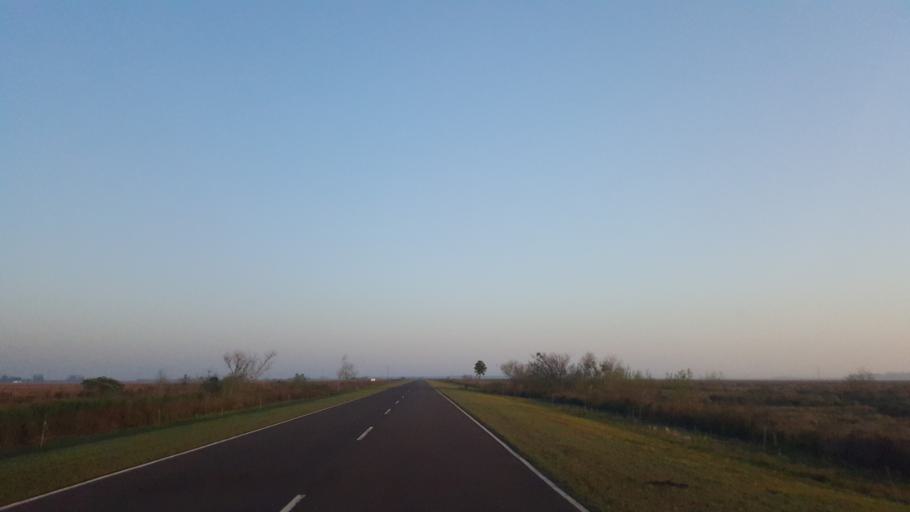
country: AR
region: Corrientes
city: Ituzaingo
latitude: -27.5802
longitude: -56.6379
